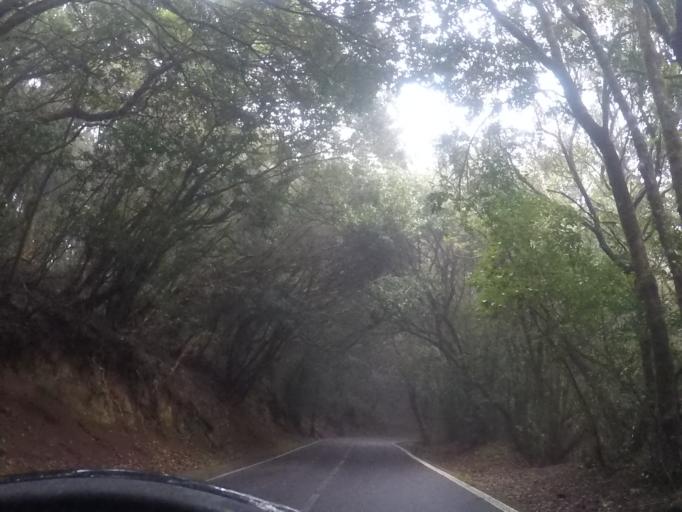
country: ES
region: Canary Islands
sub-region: Provincia de Santa Cruz de Tenerife
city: Tegueste
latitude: 28.5313
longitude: -16.2822
